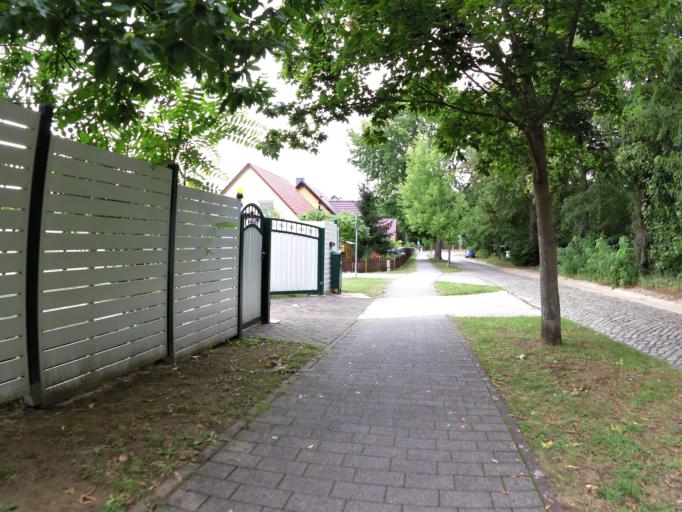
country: DE
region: Brandenburg
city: Storkow
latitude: 52.2619
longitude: 13.9589
